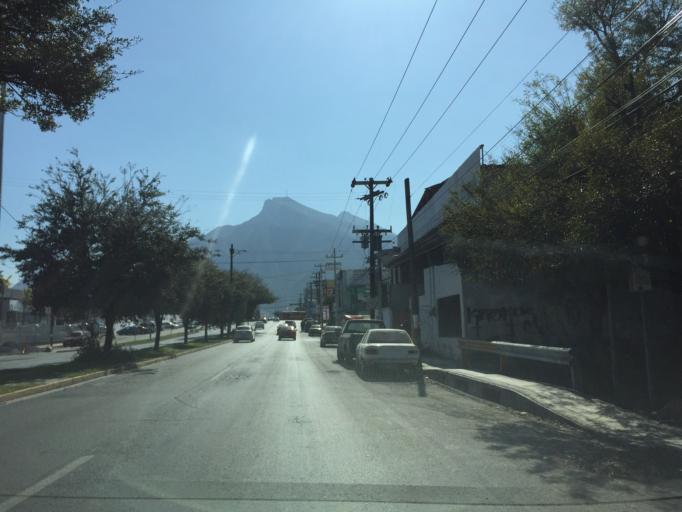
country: MX
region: Nuevo Leon
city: Guadalupe
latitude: 25.6848
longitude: -100.2304
